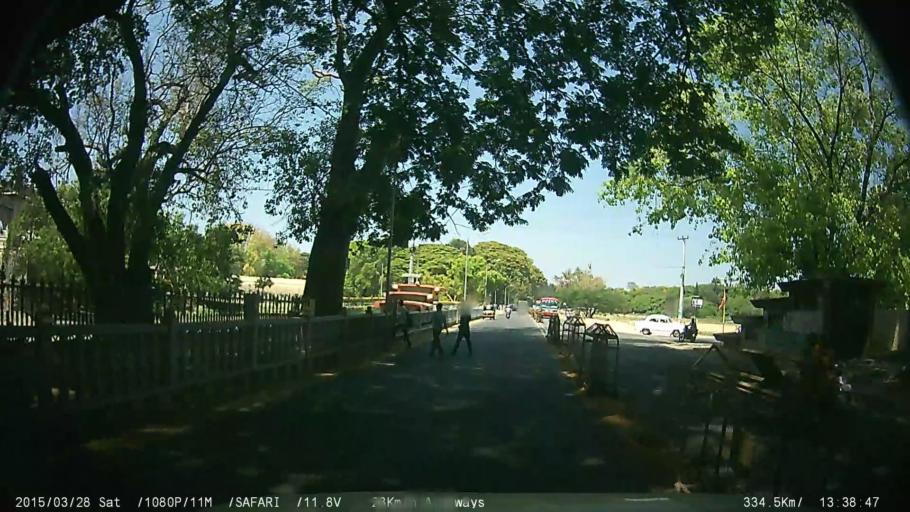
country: IN
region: Karnataka
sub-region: Mysore
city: Mysore
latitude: 12.3037
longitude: 76.6583
